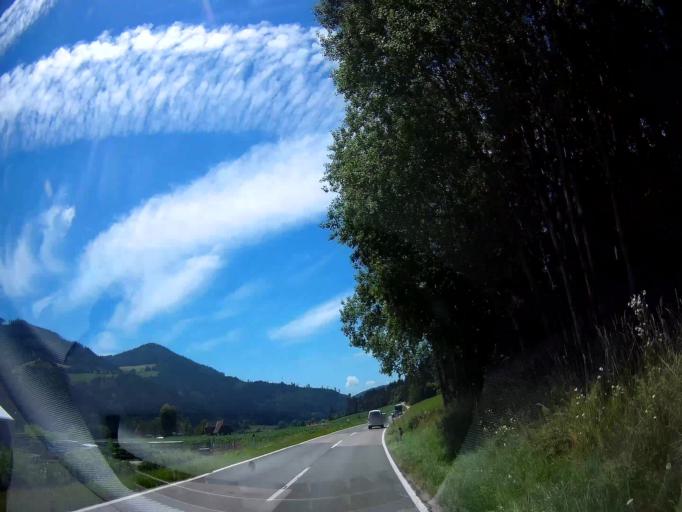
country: AT
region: Carinthia
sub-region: Politischer Bezirk Sankt Veit an der Glan
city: Strassburg
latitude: 46.8973
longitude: 14.3550
